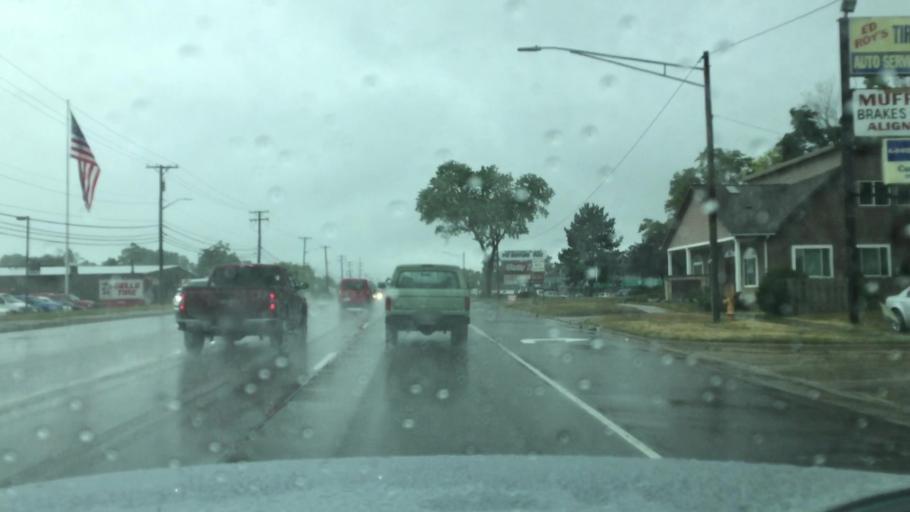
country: US
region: Michigan
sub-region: Oakland County
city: Waterford
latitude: 42.6951
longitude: -83.3927
